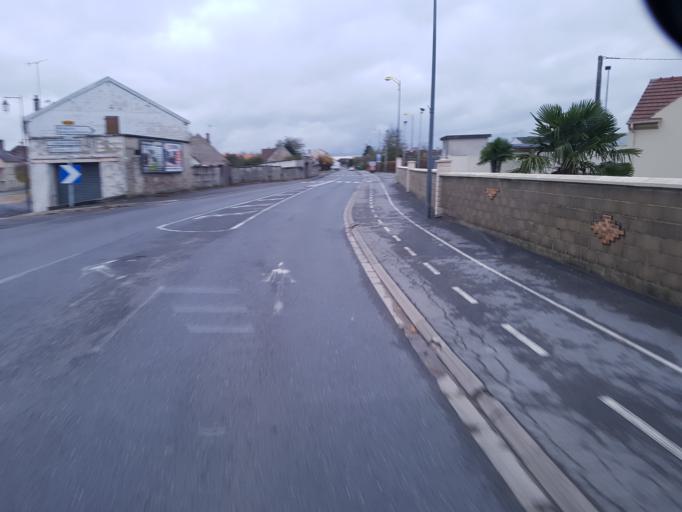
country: FR
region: Champagne-Ardenne
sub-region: Departement de la Marne
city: Montmirail
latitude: 48.8707
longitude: 3.5496
